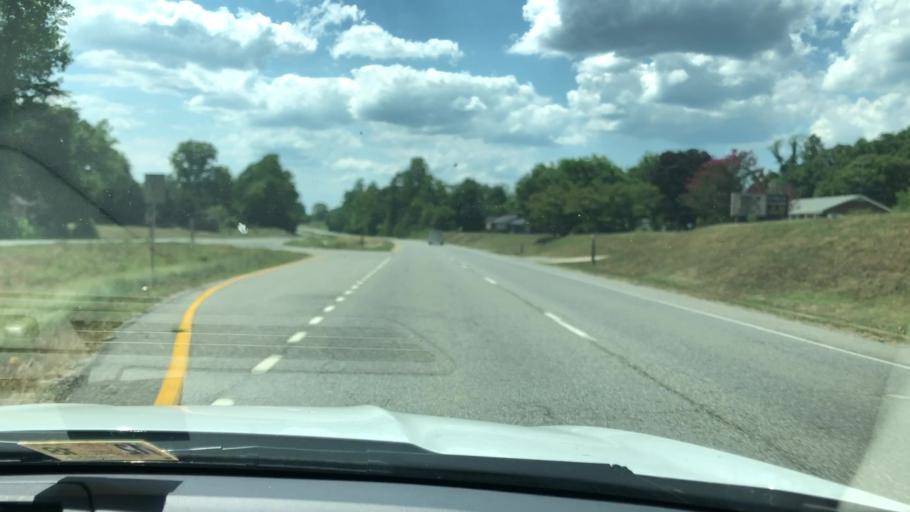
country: US
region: Virginia
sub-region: King William County
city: West Point
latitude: 37.5482
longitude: -76.7247
